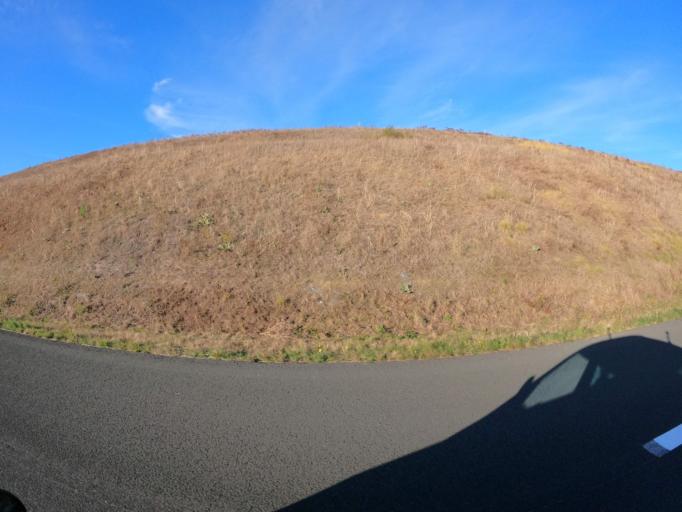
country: FR
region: Pays de la Loire
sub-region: Departement de Maine-et-Loire
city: Chemille-Melay
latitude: 47.2443
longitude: -0.6786
